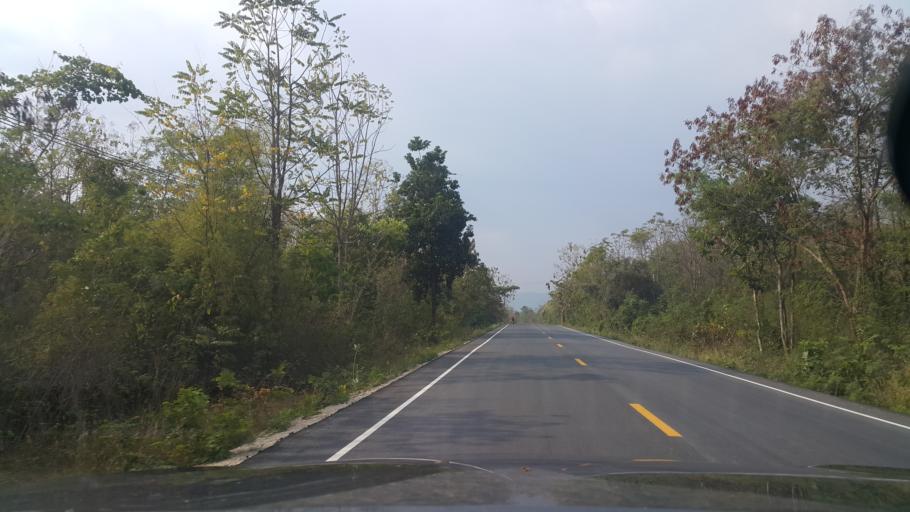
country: TH
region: Sukhothai
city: Thung Saliam
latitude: 17.2542
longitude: 99.5220
